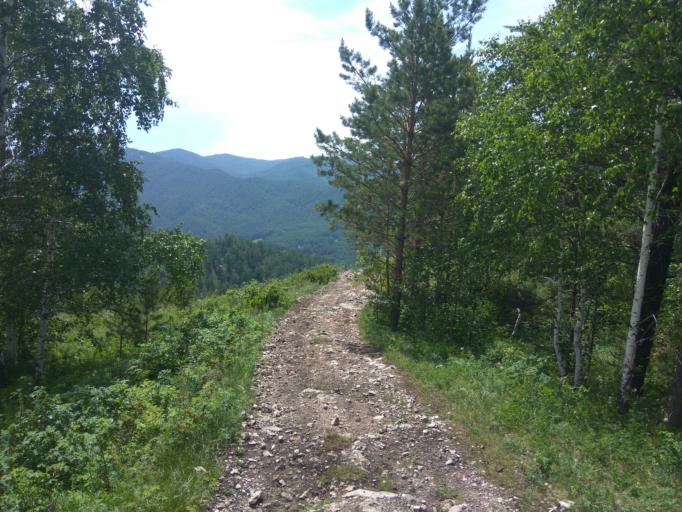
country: RU
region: Krasnoyarskiy
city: Krasnoyarsk
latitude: 55.9451
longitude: 92.8637
